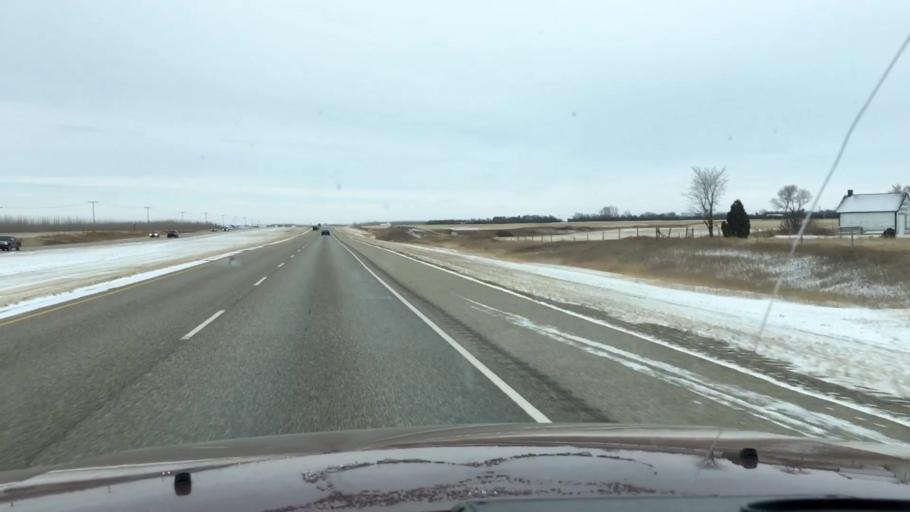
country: CA
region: Saskatchewan
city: Watrous
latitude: 51.0598
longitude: -105.8209
